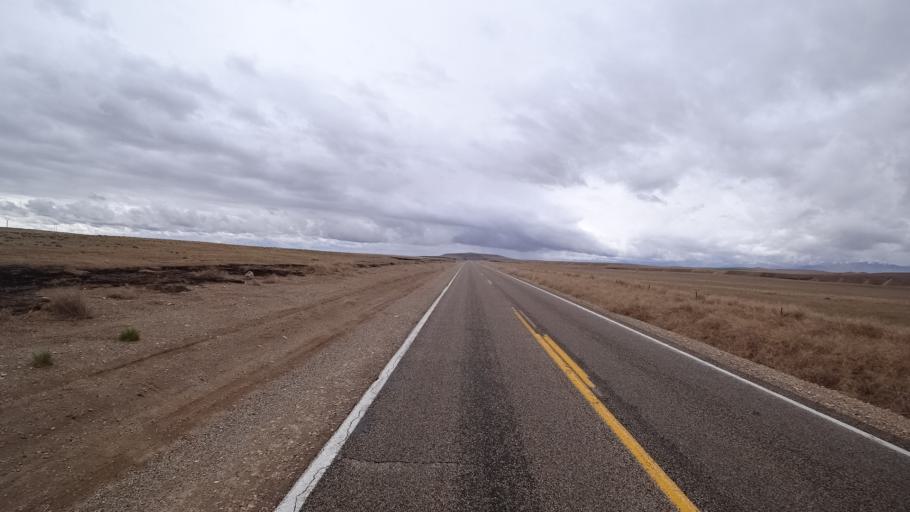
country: US
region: Idaho
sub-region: Owyhee County
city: Murphy
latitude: 43.2906
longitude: -116.3941
